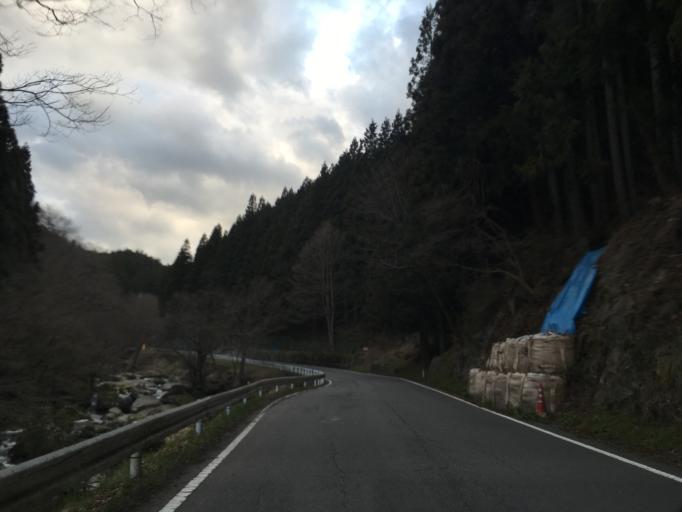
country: JP
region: Fukushima
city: Ishikawa
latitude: 37.0622
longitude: 140.5087
